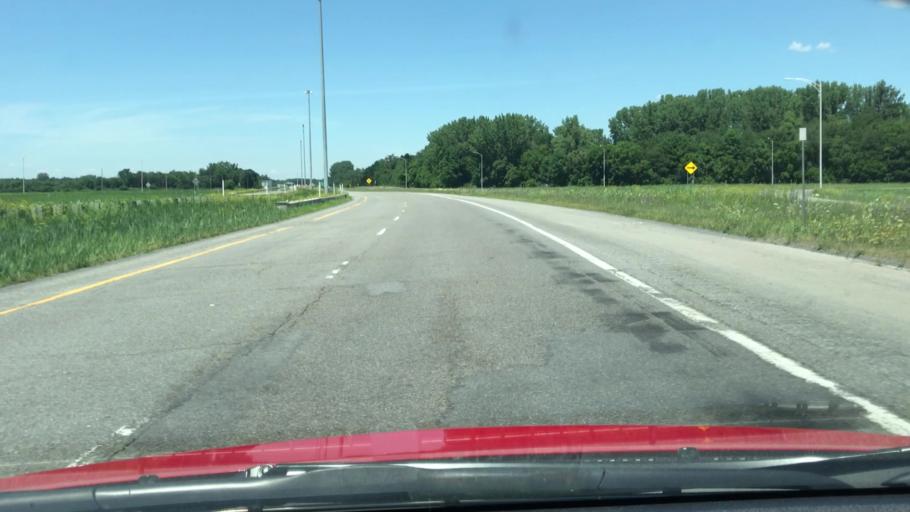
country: US
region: New York
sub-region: Clinton County
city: Champlain
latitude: 45.0689
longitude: -73.4545
